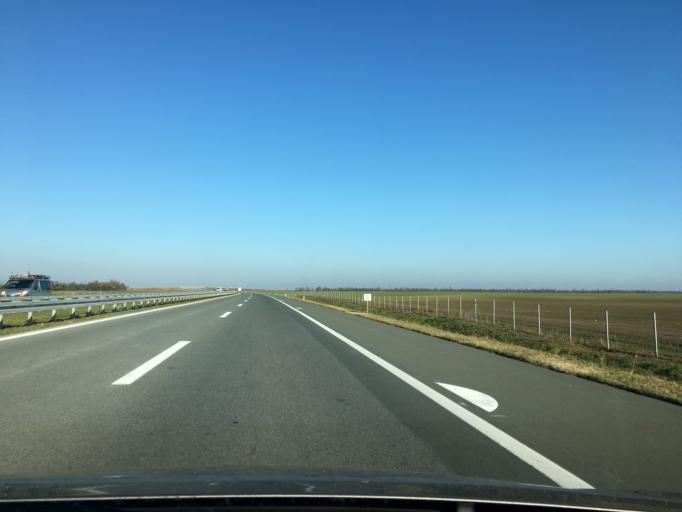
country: RS
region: Autonomna Pokrajina Vojvodina
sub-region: Severnobacki Okrug
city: Mali Igos
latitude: 45.6845
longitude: 19.7277
